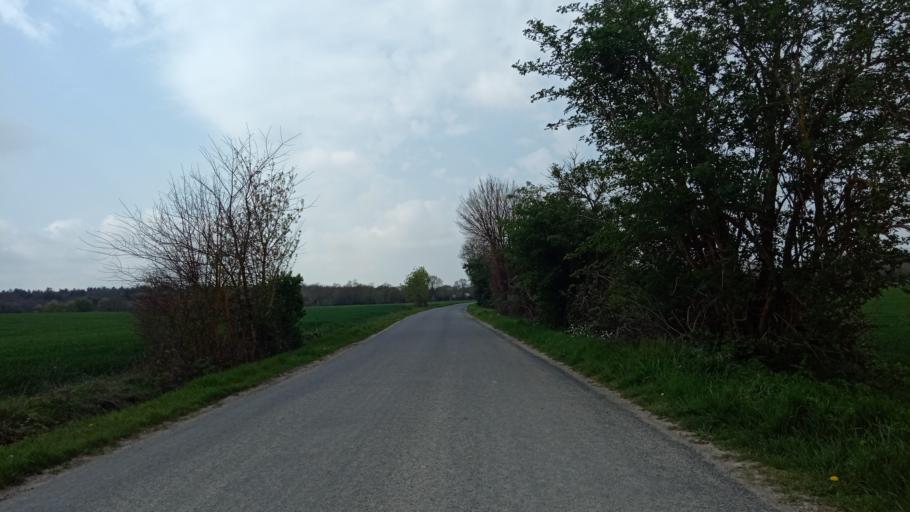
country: FR
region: Poitou-Charentes
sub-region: Departement de la Charente-Maritime
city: Verines
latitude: 46.1513
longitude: -0.9332
